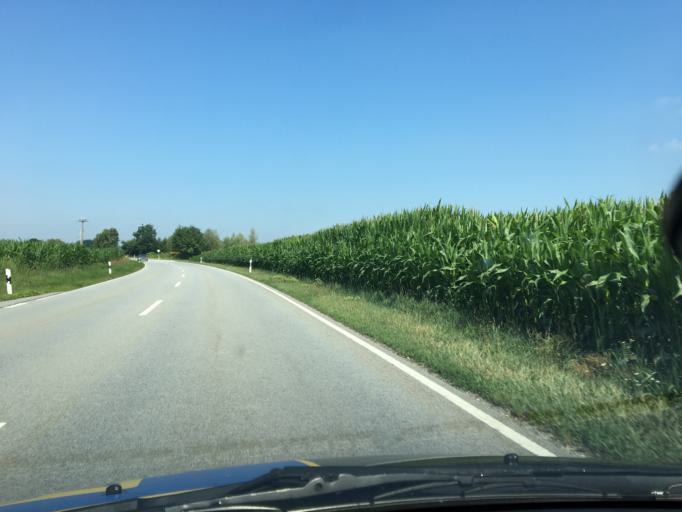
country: DE
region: Bavaria
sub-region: Upper Bavaria
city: Aresing
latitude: 48.2664
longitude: 12.6256
